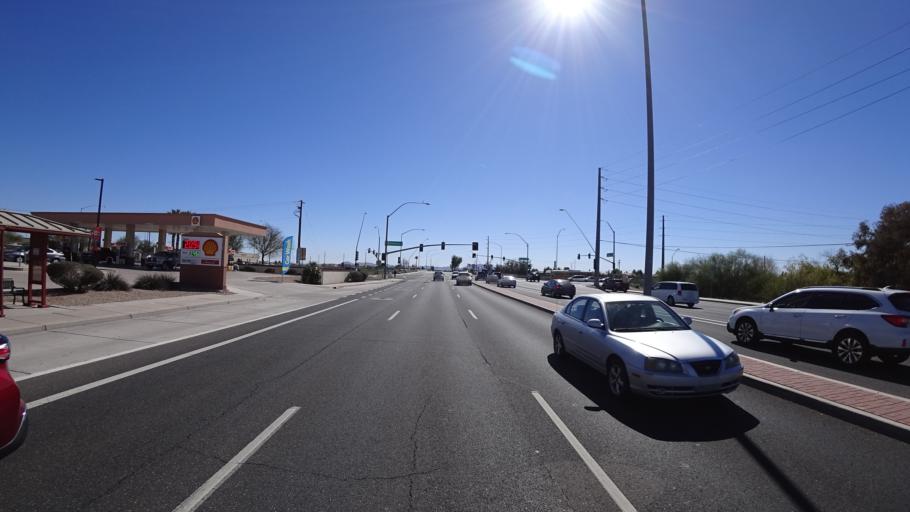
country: US
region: Arizona
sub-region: Maricopa County
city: Gilbert
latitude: 33.3657
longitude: -111.6876
